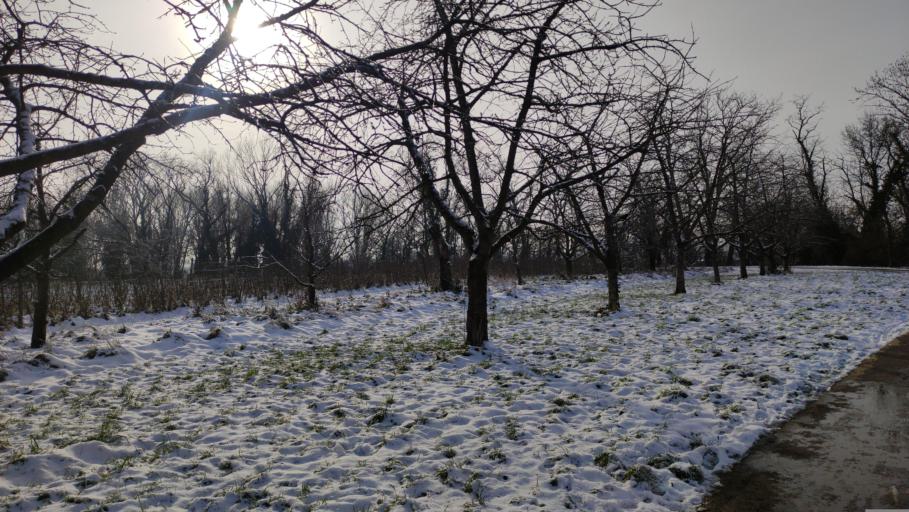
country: DE
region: Baden-Wuerttemberg
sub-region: Freiburg Region
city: Weil am Rhein
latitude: 47.6093
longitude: 7.6043
